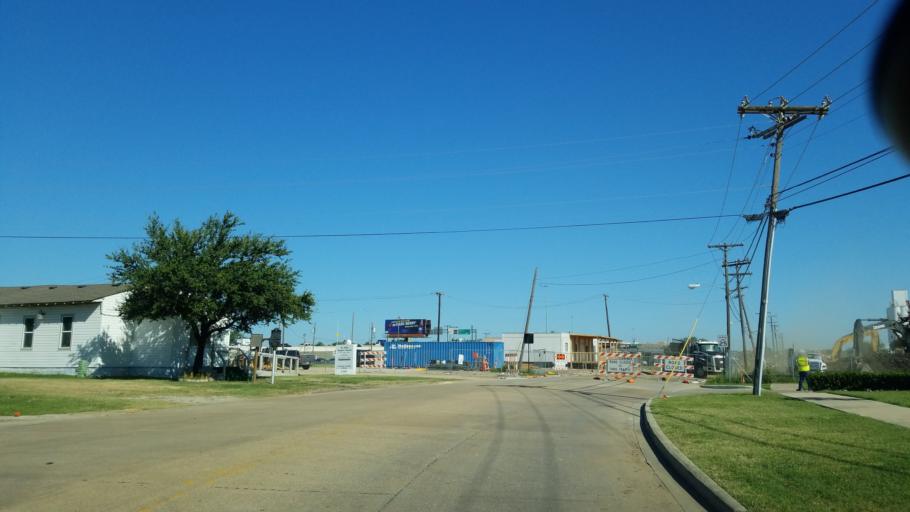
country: US
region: Texas
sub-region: Dallas County
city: Carrollton
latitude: 32.9481
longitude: -96.9048
